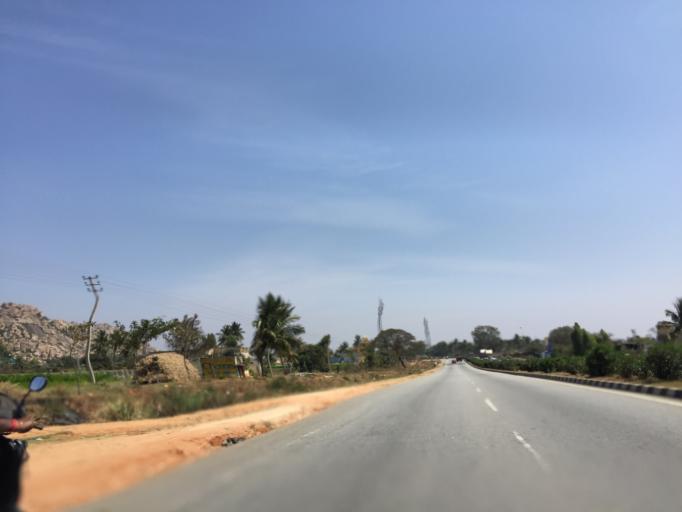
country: IN
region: Karnataka
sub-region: Kolar
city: Kolar
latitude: 13.1204
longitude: 78.0779
